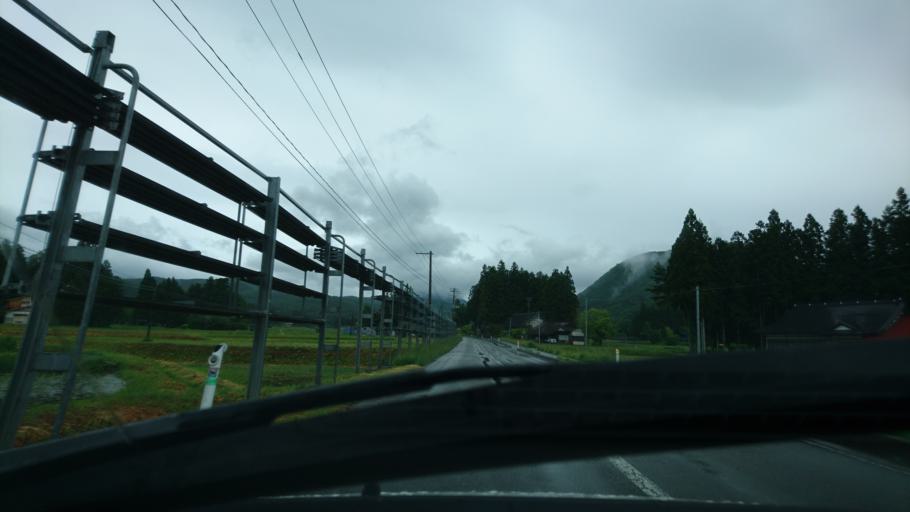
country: JP
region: Iwate
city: Ichinoseki
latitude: 38.9771
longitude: 140.9241
